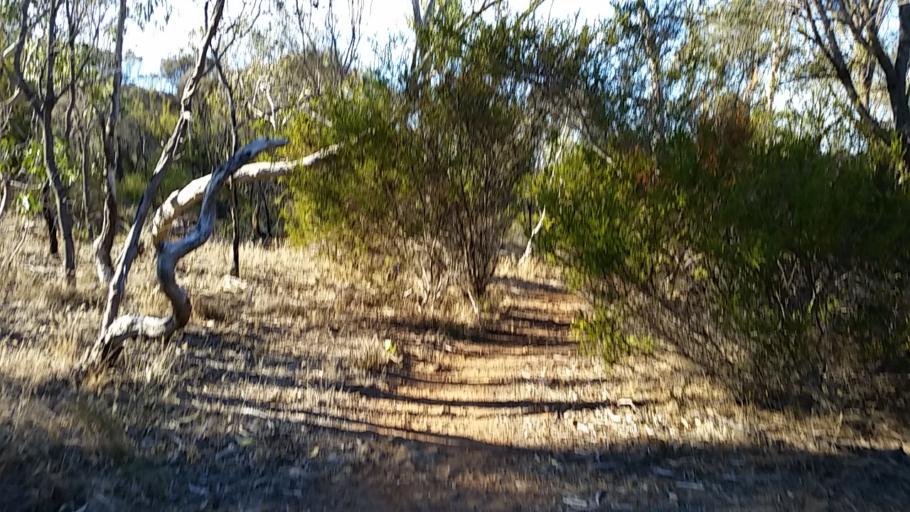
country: AU
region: South Australia
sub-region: Mount Barker
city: Nairne
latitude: -35.0665
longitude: 138.9216
